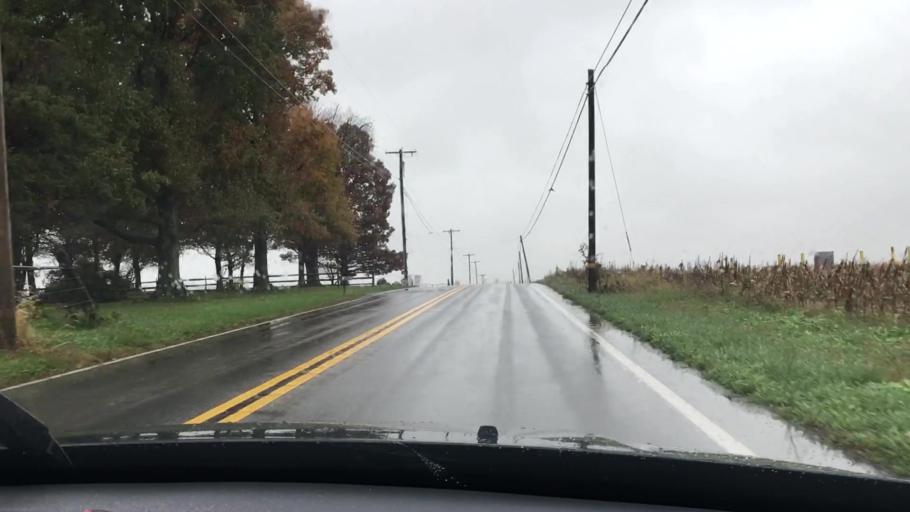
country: US
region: Maryland
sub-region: Frederick County
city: Buckeystown
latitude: 39.3108
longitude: -77.4434
